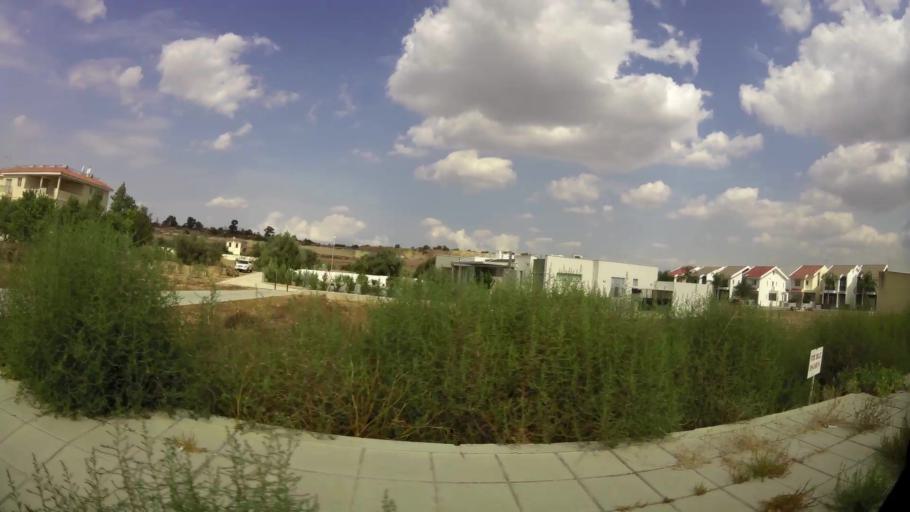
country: CY
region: Lefkosia
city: Geri
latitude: 35.1156
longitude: 33.3695
